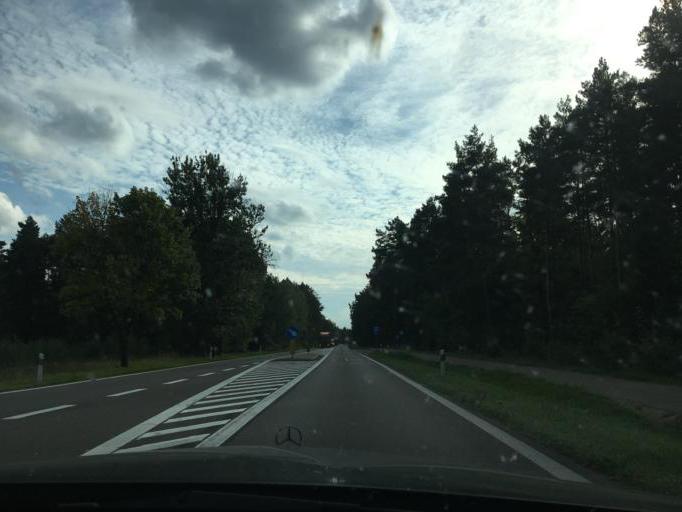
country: PL
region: Podlasie
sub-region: Powiat grajewski
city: Rajgrod
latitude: 53.7137
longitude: 22.6726
